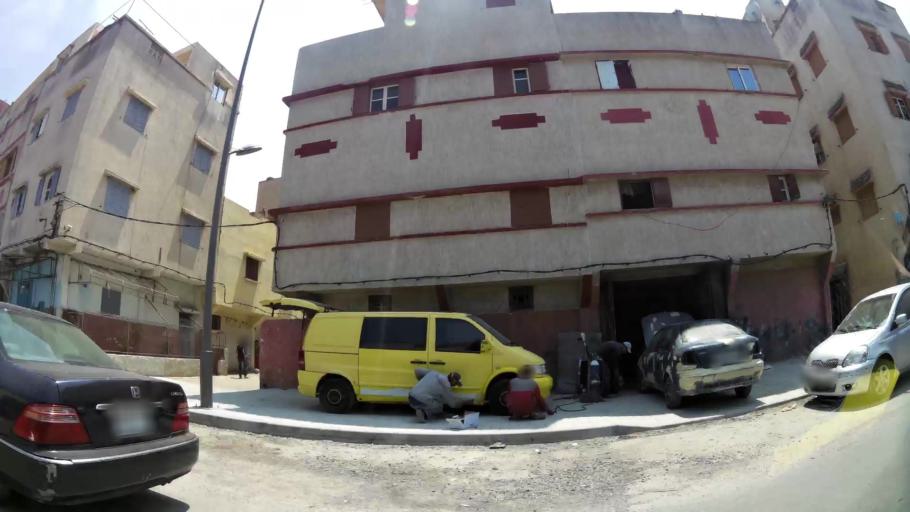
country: MA
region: Rabat-Sale-Zemmour-Zaer
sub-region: Rabat
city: Rabat
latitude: 33.9856
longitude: -6.8821
